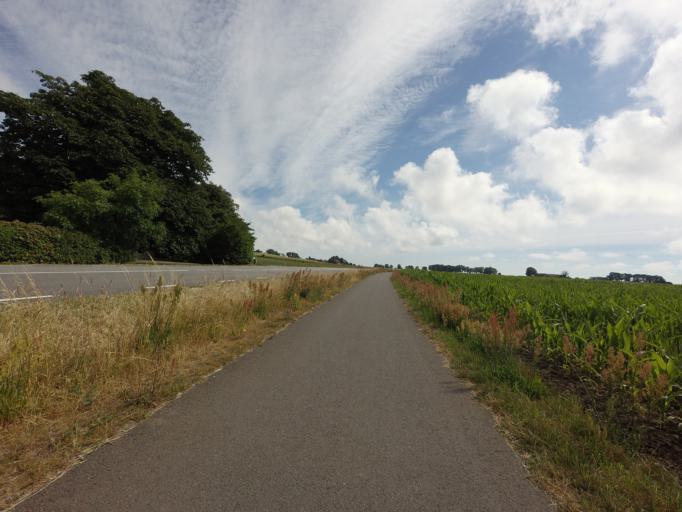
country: SE
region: Skane
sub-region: Simrishamns Kommun
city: Simrishamn
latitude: 55.4876
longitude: 14.3003
